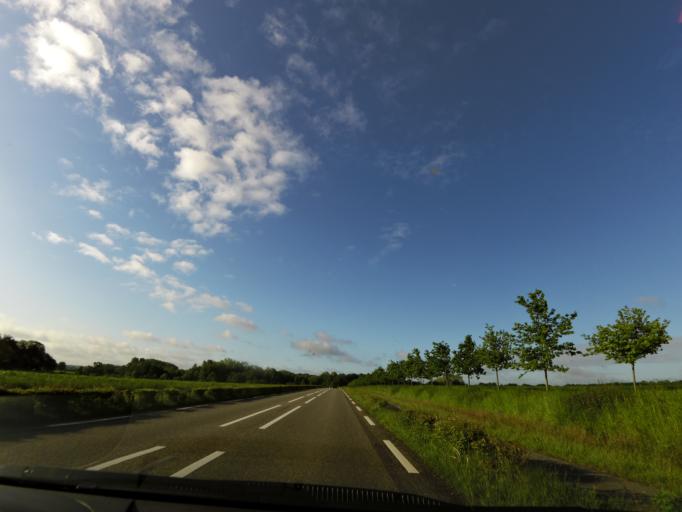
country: NL
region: Limburg
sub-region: Gemeente Voerendaal
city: Voerendaal
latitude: 50.8945
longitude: 5.9269
